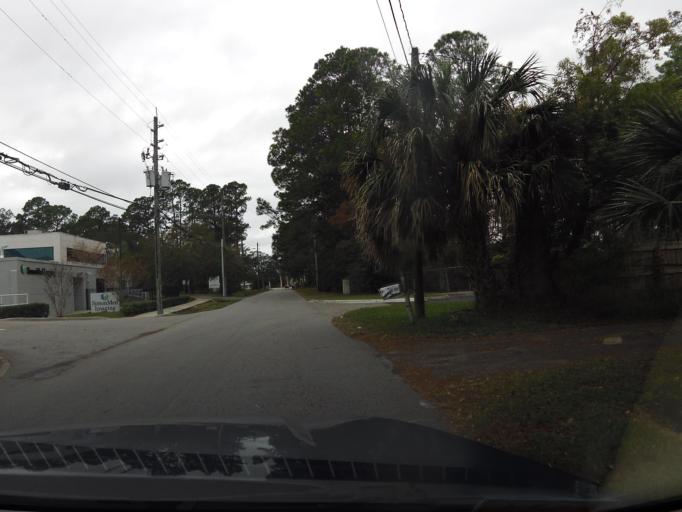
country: US
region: Florida
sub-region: Duval County
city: Jacksonville
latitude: 30.2837
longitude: -81.5999
